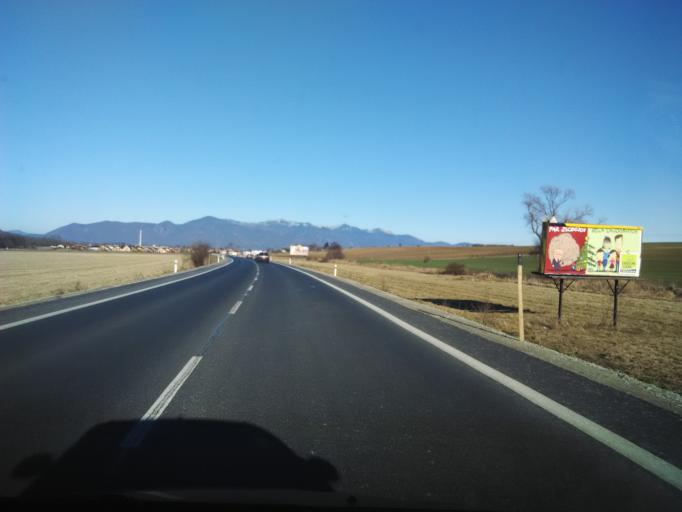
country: SK
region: Zilinsky
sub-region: Okres Martin
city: Martin
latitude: 49.0131
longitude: 18.8985
